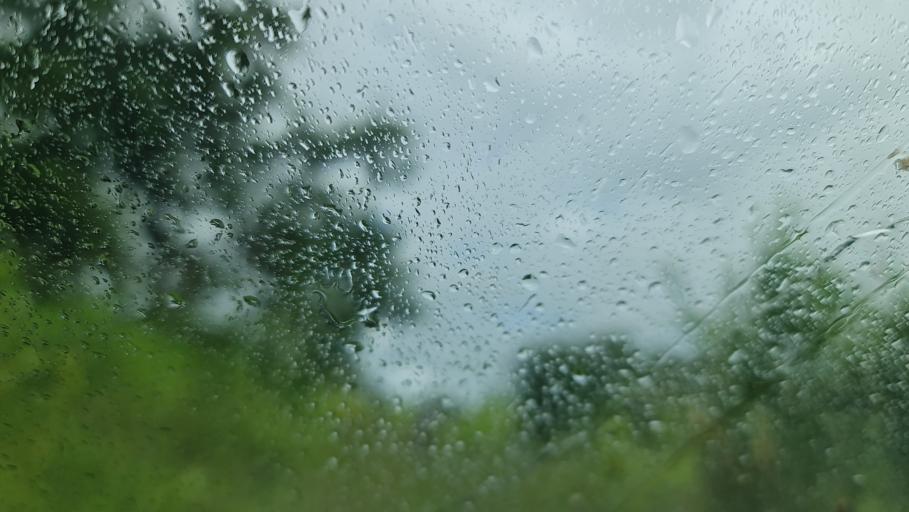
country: MW
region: Southern Region
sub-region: Nsanje District
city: Nsanje
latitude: -17.4461
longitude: 35.8437
